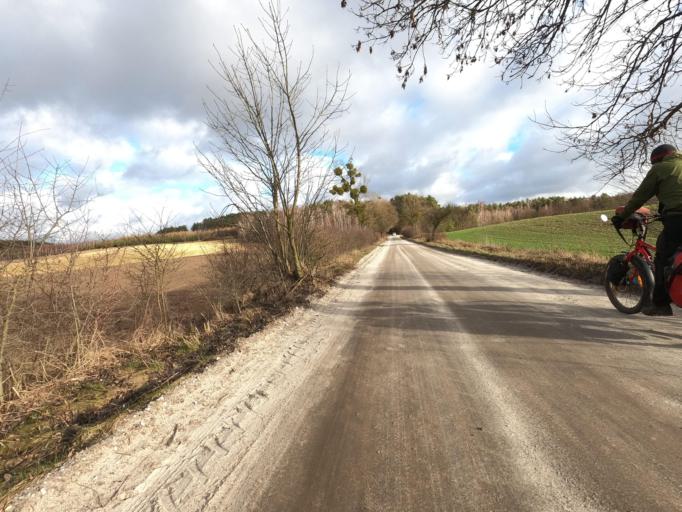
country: PL
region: Greater Poland Voivodeship
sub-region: Powiat pilski
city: Miasteczko Krajenskie
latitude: 53.1018
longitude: 17.0440
